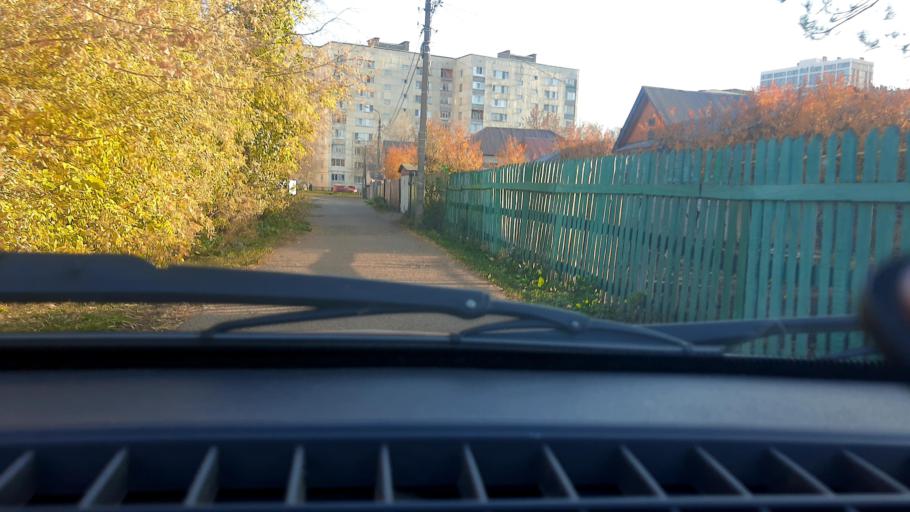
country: RU
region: Bashkortostan
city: Avdon
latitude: 54.6997
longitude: 55.8268
